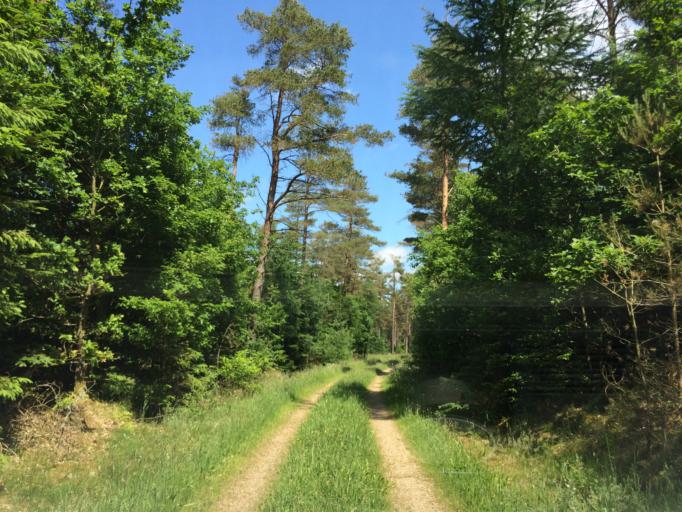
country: DK
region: Central Jutland
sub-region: Holstebro Kommune
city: Ulfborg
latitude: 56.2138
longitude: 8.4379
